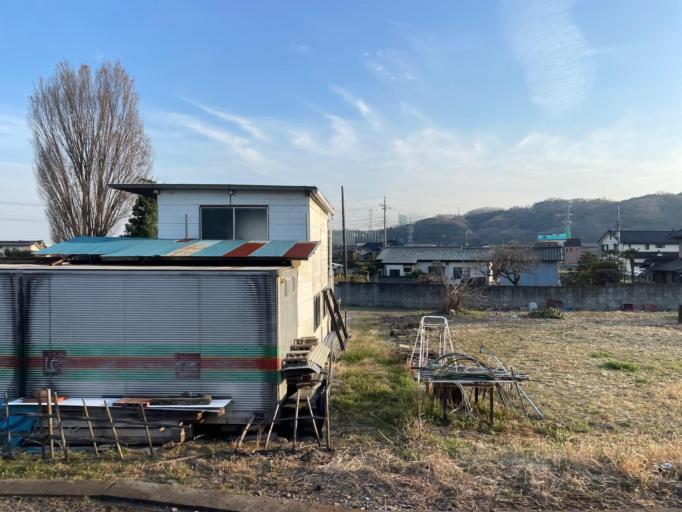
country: JP
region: Gunma
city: Takasaki
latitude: 36.3380
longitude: 138.9722
